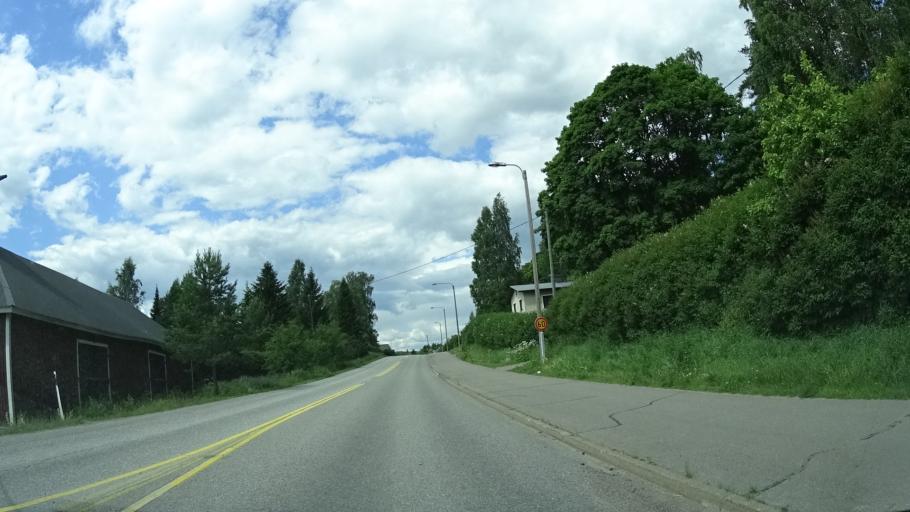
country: FI
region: Uusimaa
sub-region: Helsinki
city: Nurmijaervi
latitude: 60.3837
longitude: 24.6512
